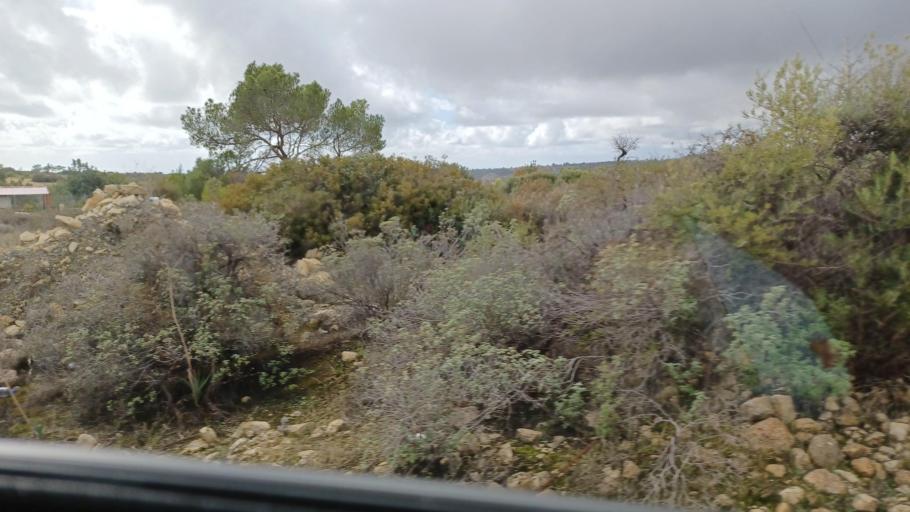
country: CY
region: Limassol
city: Sotira
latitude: 34.7328
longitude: 32.8624
